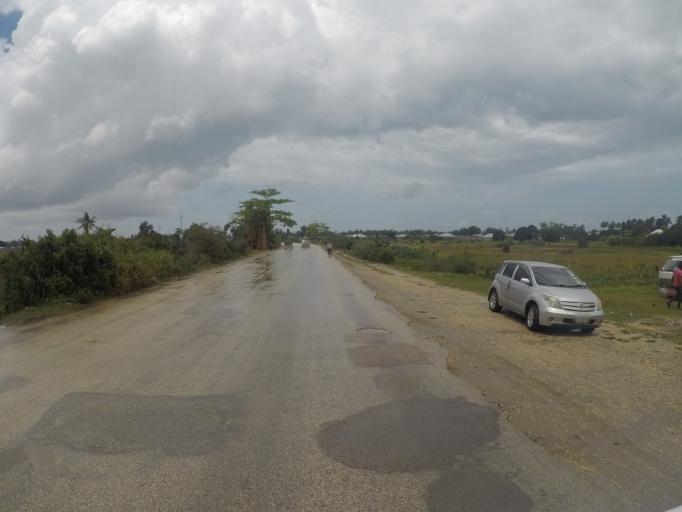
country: TZ
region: Zanzibar Central/South
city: Koani
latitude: -6.0758
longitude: 39.2230
